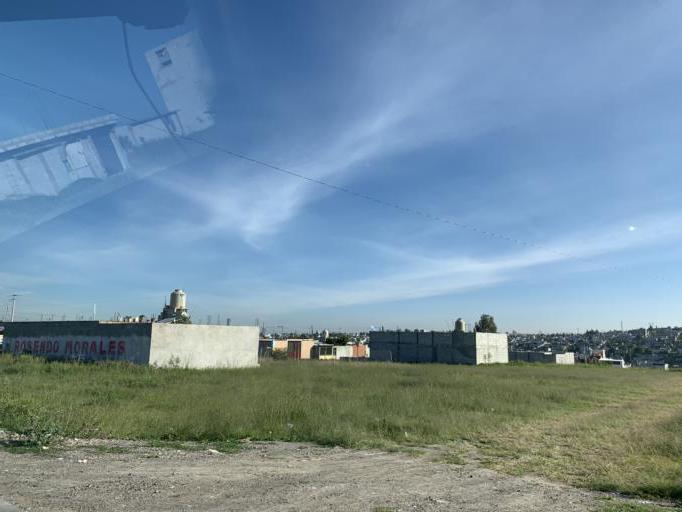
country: MX
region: Puebla
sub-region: Puebla
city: El Capulo (La Quebradora)
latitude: 18.9493
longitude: -98.2626
